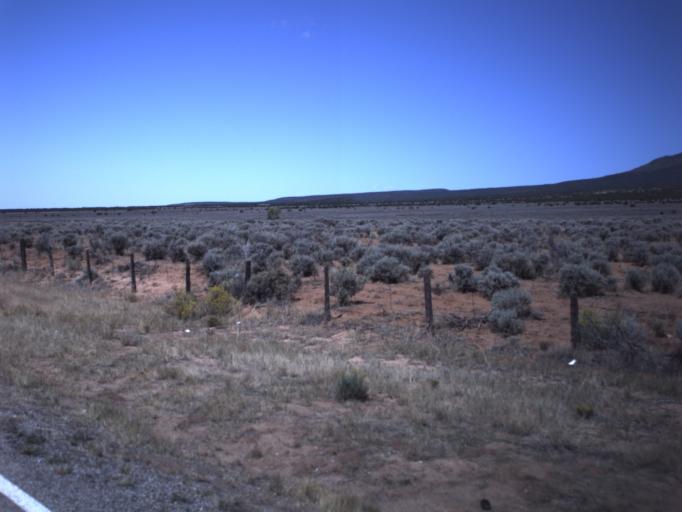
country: US
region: Utah
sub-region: Grand County
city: Moab
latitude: 38.3111
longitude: -109.2981
